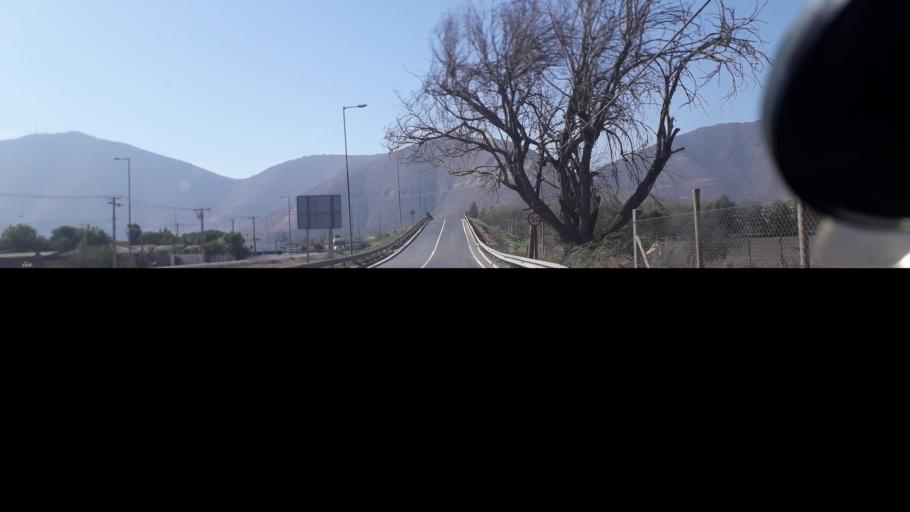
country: CL
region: Valparaiso
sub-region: Provincia de San Felipe
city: Llaillay
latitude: -32.8529
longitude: -70.9435
